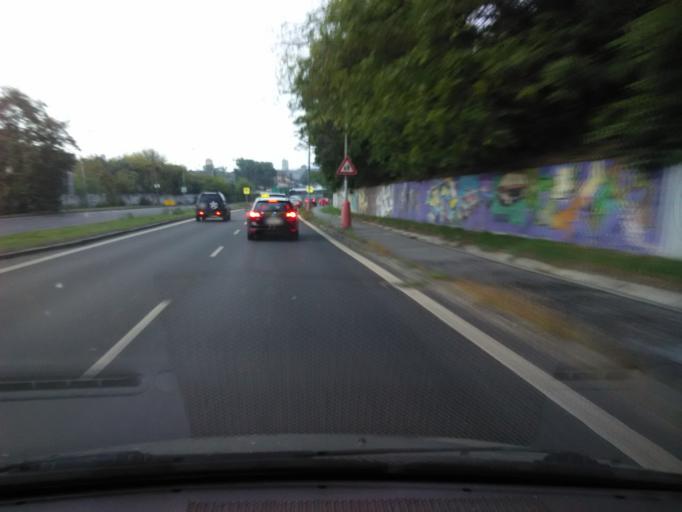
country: SK
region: Nitriansky
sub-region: Okres Nitra
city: Nitra
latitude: 48.2976
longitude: 18.0806
